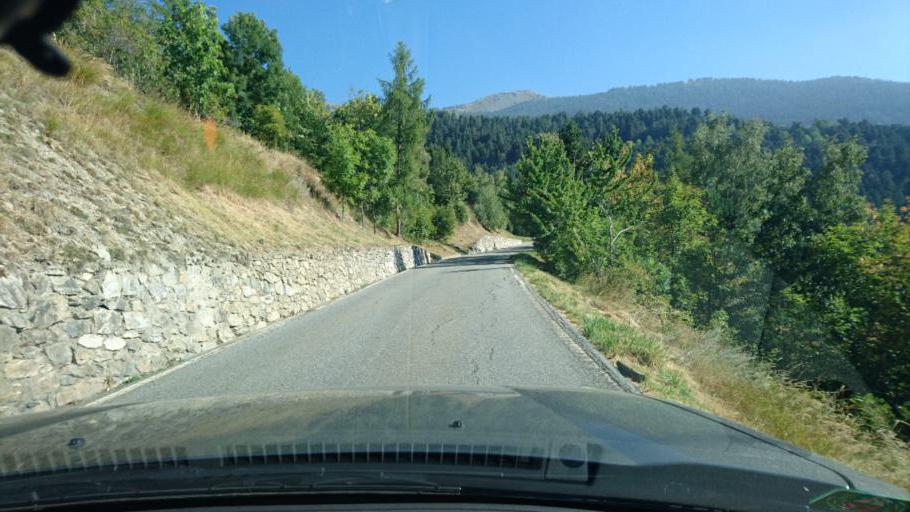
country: IT
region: Aosta Valley
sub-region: Valle d'Aosta
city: Villeneuve
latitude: 45.7278
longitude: 7.2027
